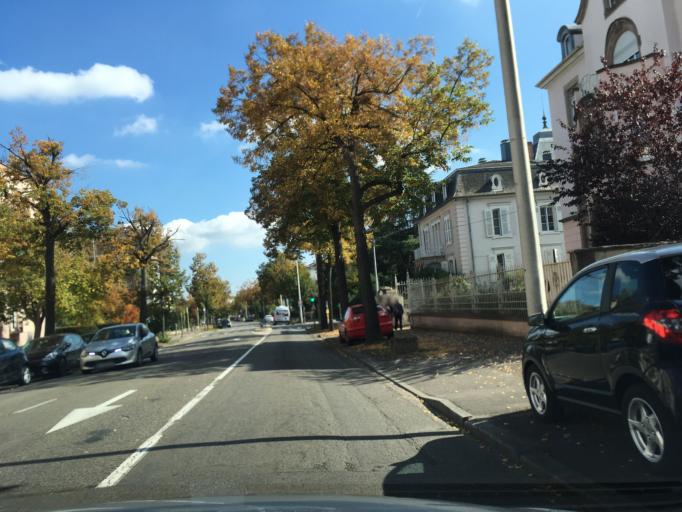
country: FR
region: Alsace
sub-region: Departement du Haut-Rhin
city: Colmar
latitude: 48.0700
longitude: 7.3540
